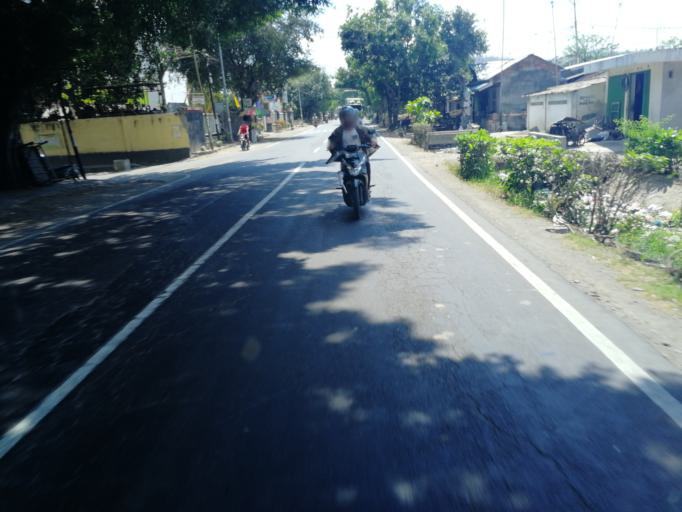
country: ID
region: West Nusa Tenggara
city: Jelateng Timur
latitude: -8.7028
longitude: 116.0944
